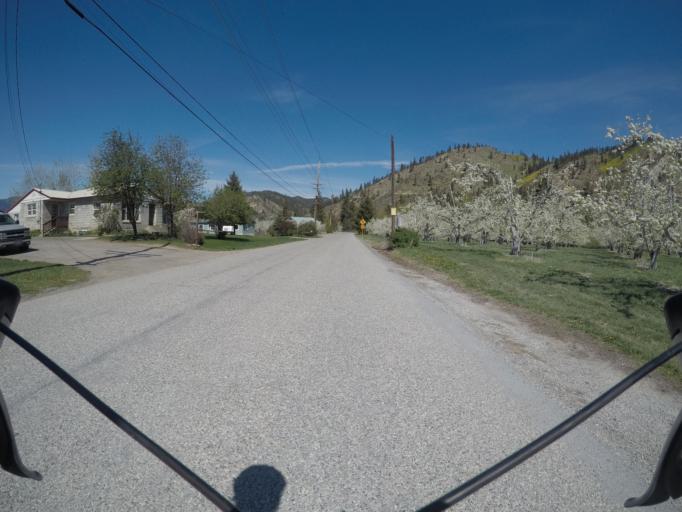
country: US
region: Washington
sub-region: Chelan County
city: Leavenworth
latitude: 47.5624
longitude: -120.5824
